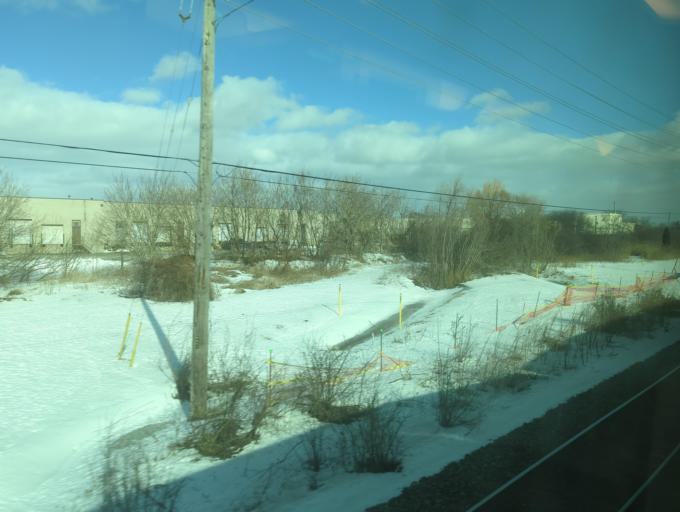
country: CA
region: Ontario
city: Oakville
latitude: 43.4457
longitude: -79.6921
